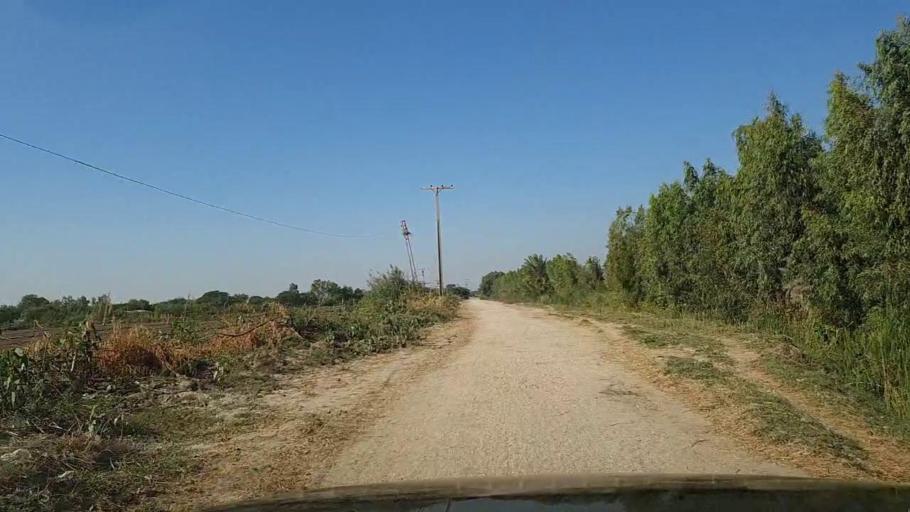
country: PK
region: Sindh
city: Thatta
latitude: 24.7090
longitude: 67.9184
